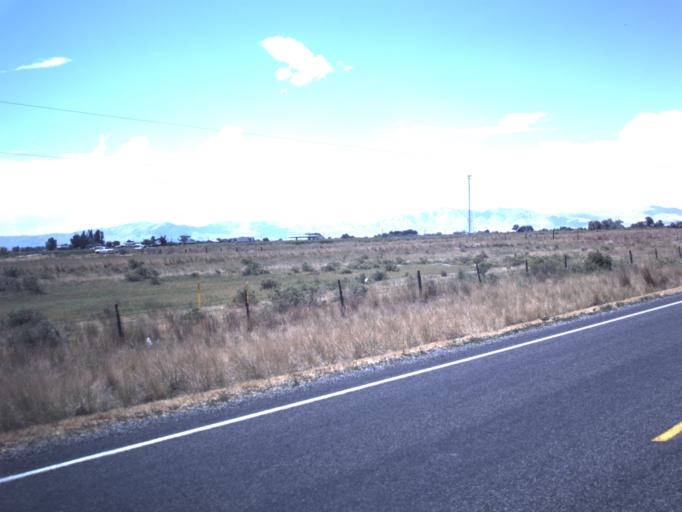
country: US
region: Utah
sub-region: Box Elder County
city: Honeyville
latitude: 41.5629
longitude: -112.1663
